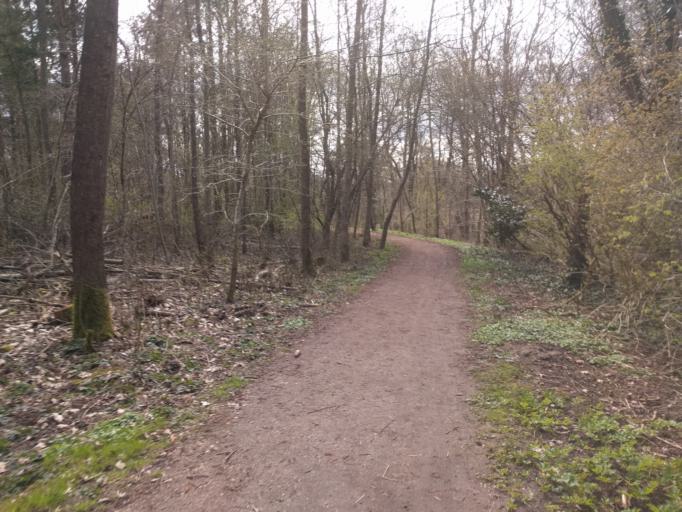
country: DK
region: South Denmark
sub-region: Odense Kommune
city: Neder Holluf
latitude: 55.3857
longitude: 10.4651
